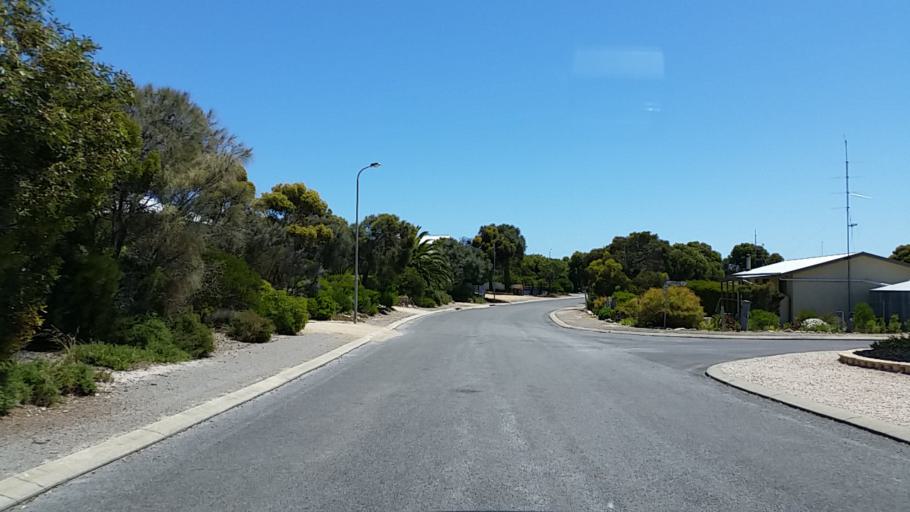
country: AU
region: South Australia
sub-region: Yorke Peninsula
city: Honiton
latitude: -35.2480
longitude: 136.9741
